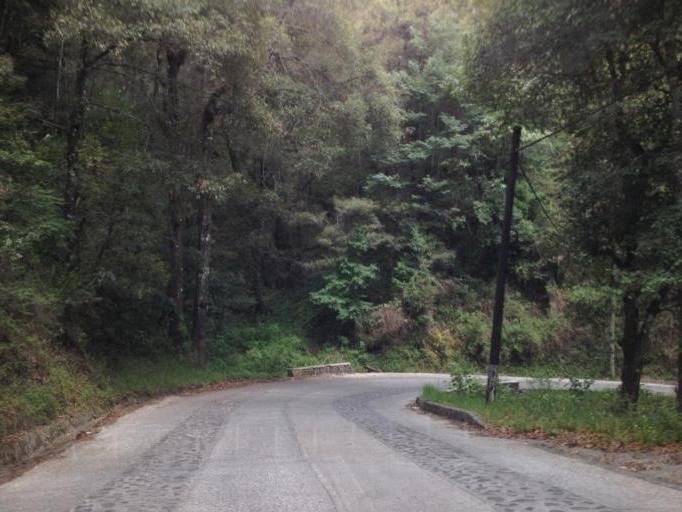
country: MX
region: Hidalgo
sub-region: Pachuca de Soto
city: San Miguel Cerezo (El Cerezo)
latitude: 20.2170
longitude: -98.7224
